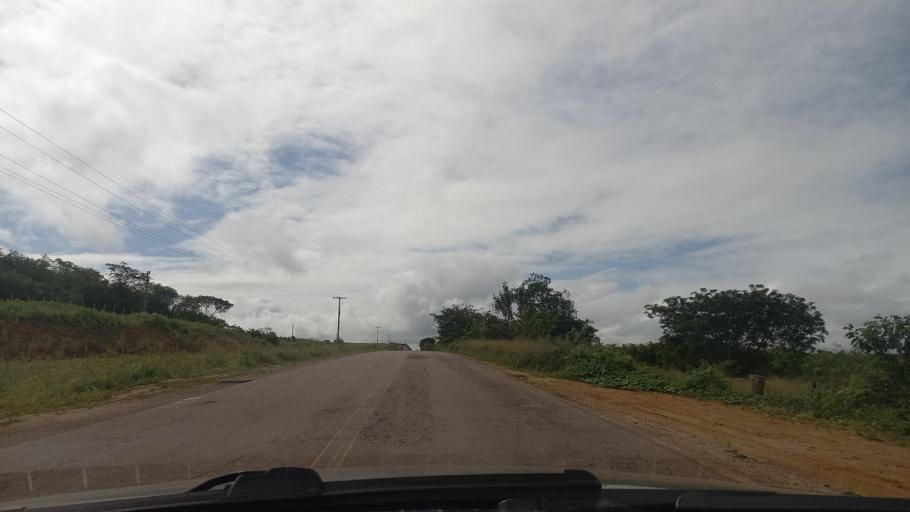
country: BR
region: Alagoas
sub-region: Batalha
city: Batalha
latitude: -9.6637
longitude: -37.1679
